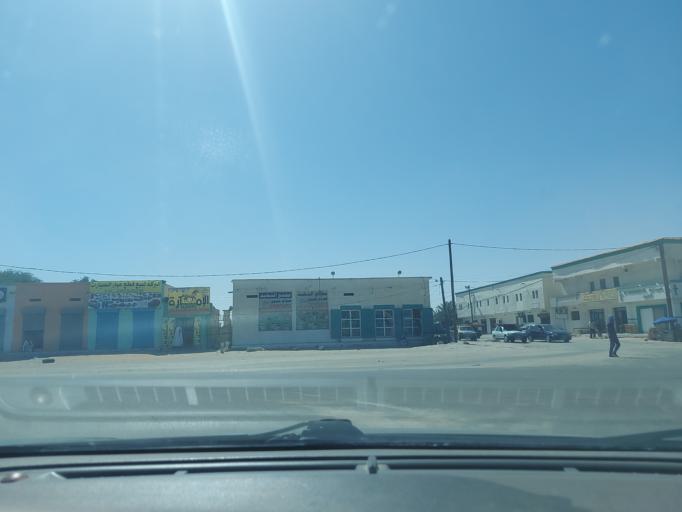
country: MR
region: Nouakchott
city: Nouakchott
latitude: 18.0604
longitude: -15.9734
